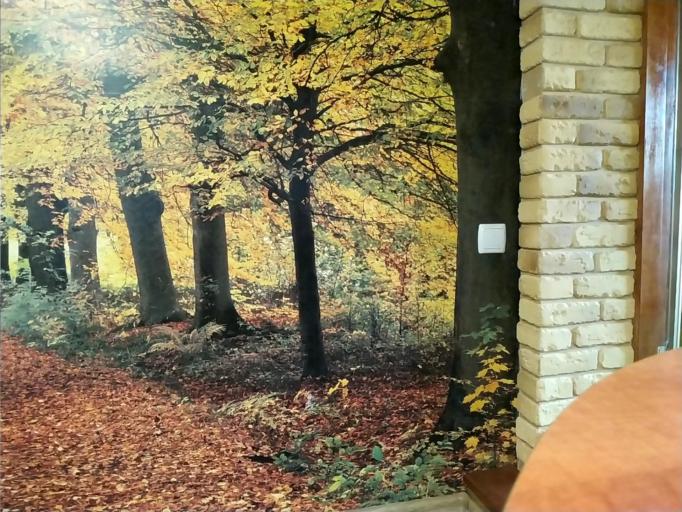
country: RU
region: Leningrad
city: Tolmachevo
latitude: 58.9310
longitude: 29.7155
